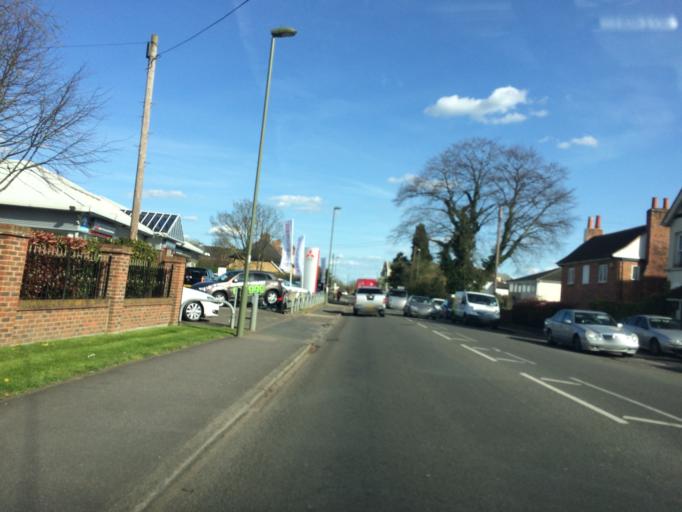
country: GB
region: England
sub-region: Surrey
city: Chertsey
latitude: 51.3896
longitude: -0.4910
